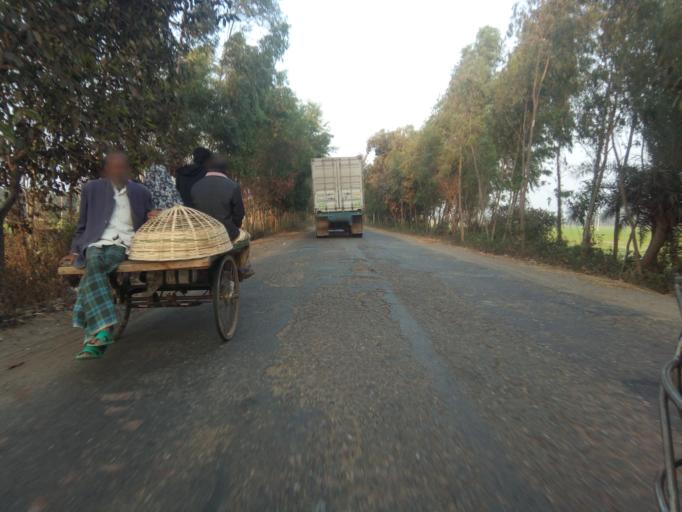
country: BD
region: Rajshahi
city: Bogra
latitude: 24.5594
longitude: 89.2011
